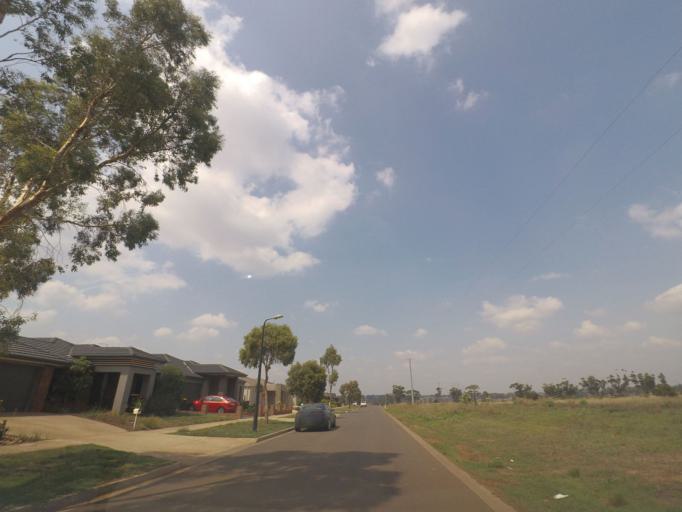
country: AU
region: Victoria
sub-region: Melton
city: Brookfield
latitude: -37.7106
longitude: 144.5447
